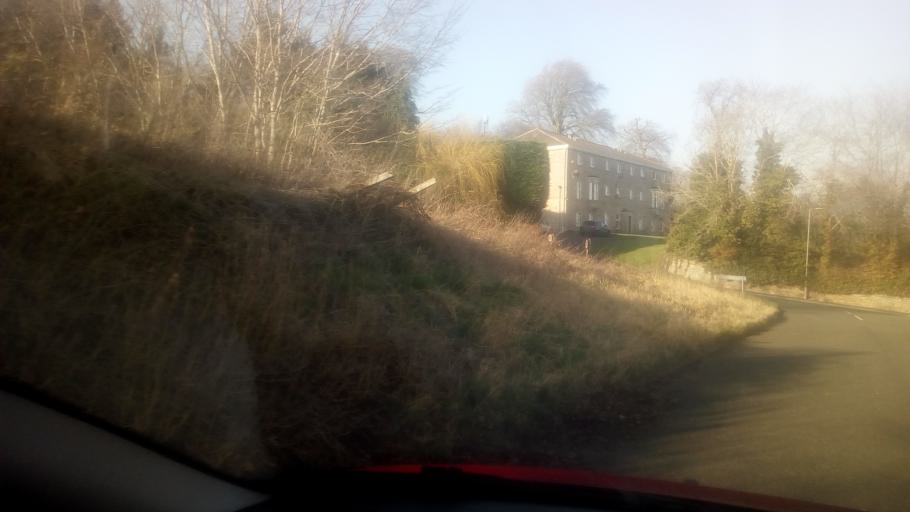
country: GB
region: Scotland
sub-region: The Scottish Borders
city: Jedburgh
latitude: 55.4776
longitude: -2.5601
